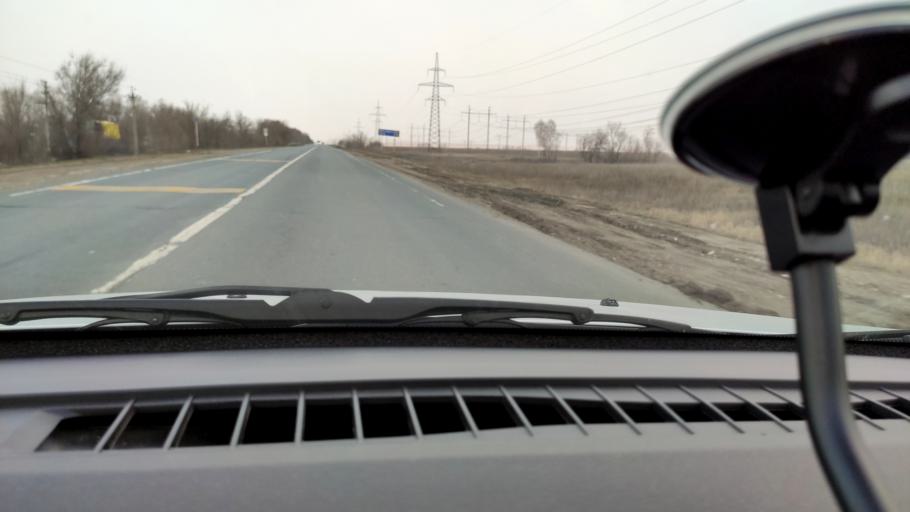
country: RU
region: Samara
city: Dubovyy Umet
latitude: 53.0716
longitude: 50.3830
